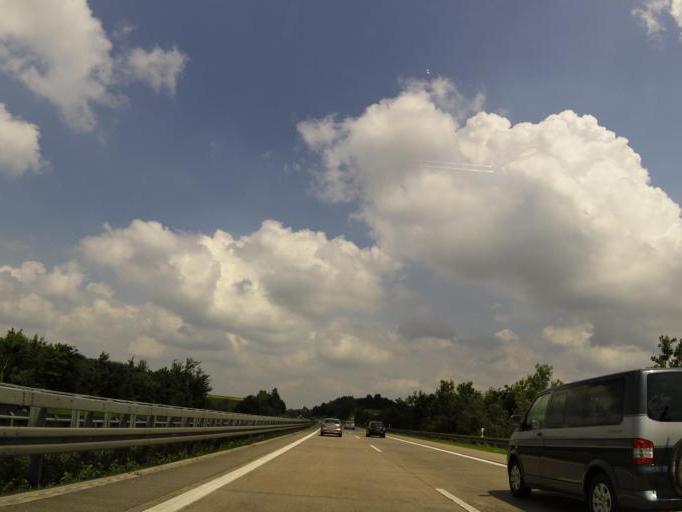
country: DE
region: Baden-Wuerttemberg
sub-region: Regierungsbezirk Stuttgart
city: Westhausen
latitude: 48.9026
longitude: 10.1809
